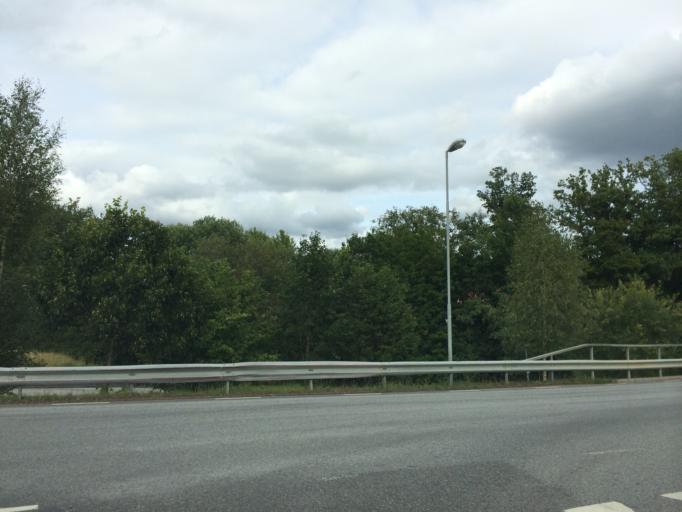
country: SE
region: Stockholm
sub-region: Sollentuna Kommun
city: Sollentuna
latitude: 59.4583
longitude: 17.9020
